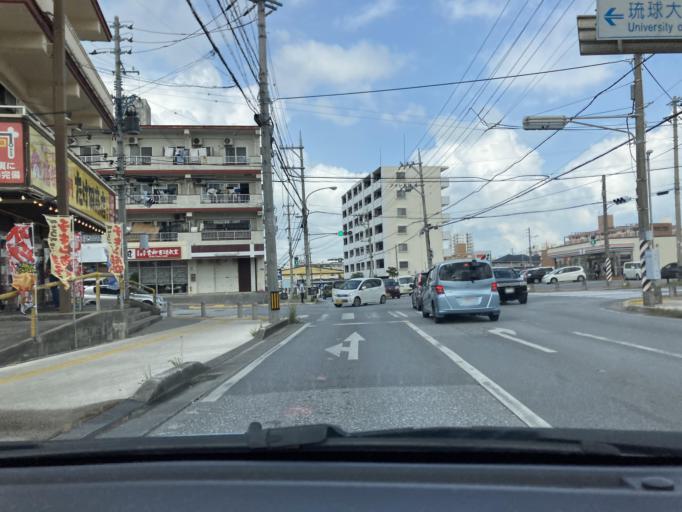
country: JP
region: Okinawa
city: Ginowan
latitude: 26.2466
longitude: 127.7702
